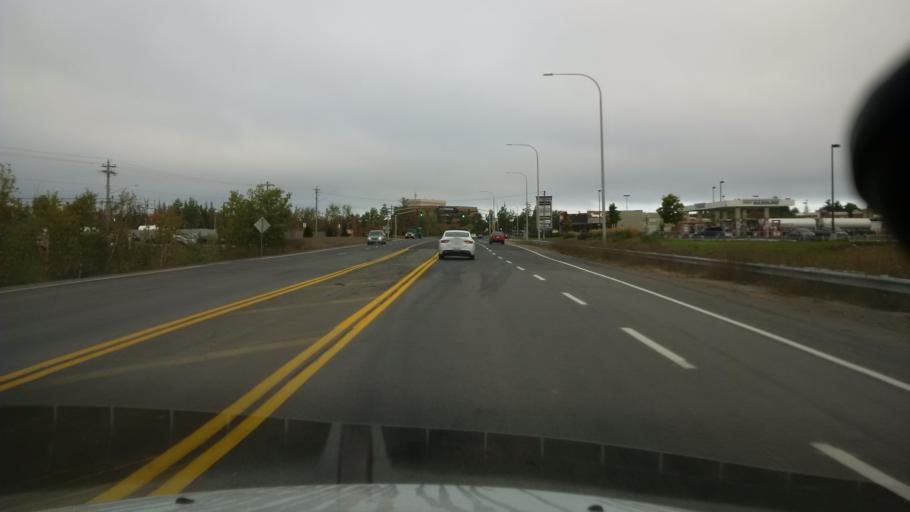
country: CA
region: New Brunswick
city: Fredericton
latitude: 45.9274
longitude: -66.6654
